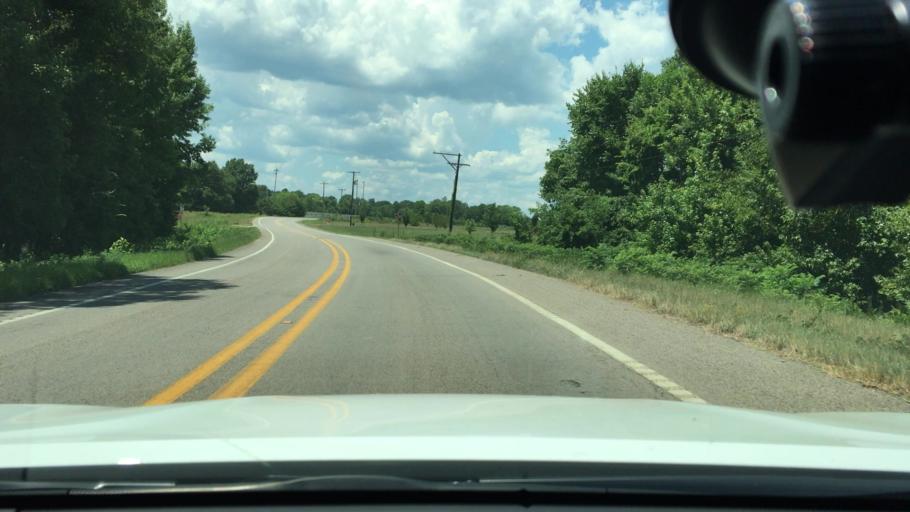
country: US
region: Arkansas
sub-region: Logan County
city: Booneville
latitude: 35.1499
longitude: -93.8320
